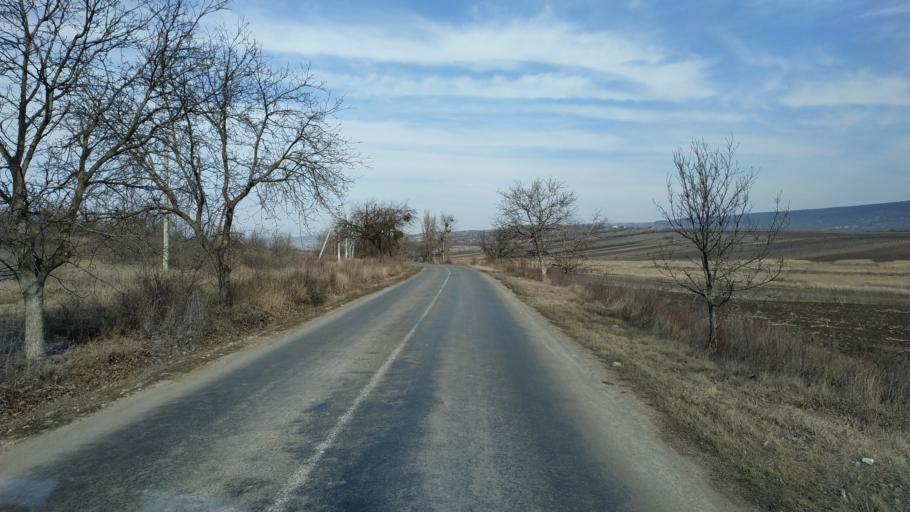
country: MD
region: Nisporeni
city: Nisporeni
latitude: 47.1295
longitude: 28.1212
